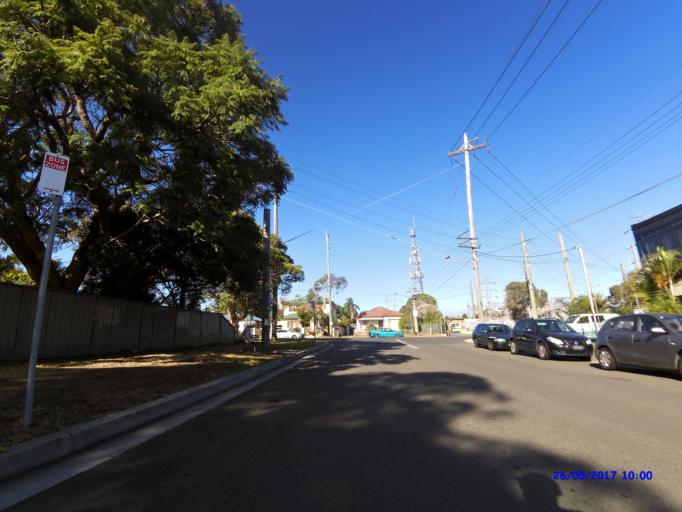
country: AU
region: New South Wales
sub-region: Sutherland Shire
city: Gymea
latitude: -34.0260
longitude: 151.0811
